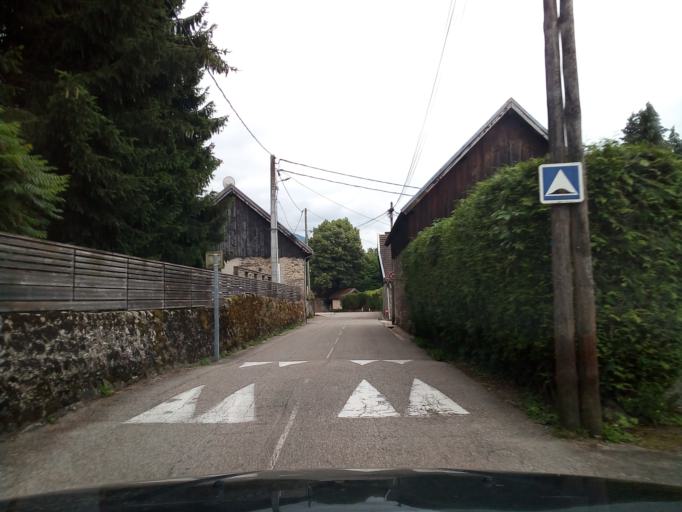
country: FR
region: Rhone-Alpes
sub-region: Departement de l'Isere
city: Vaulnaveys-le-Haut
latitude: 45.1351
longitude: 5.8363
